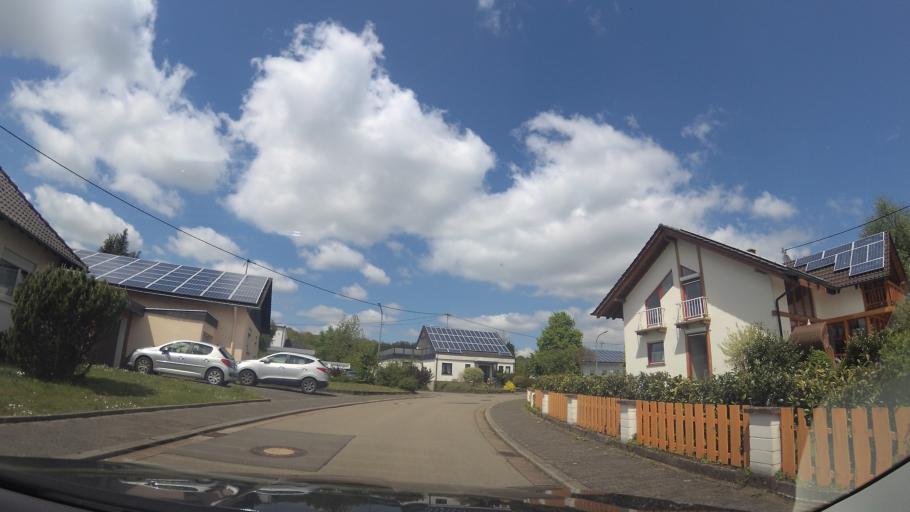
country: DE
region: Saarland
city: Eppelborn
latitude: 49.4498
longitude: 6.9632
